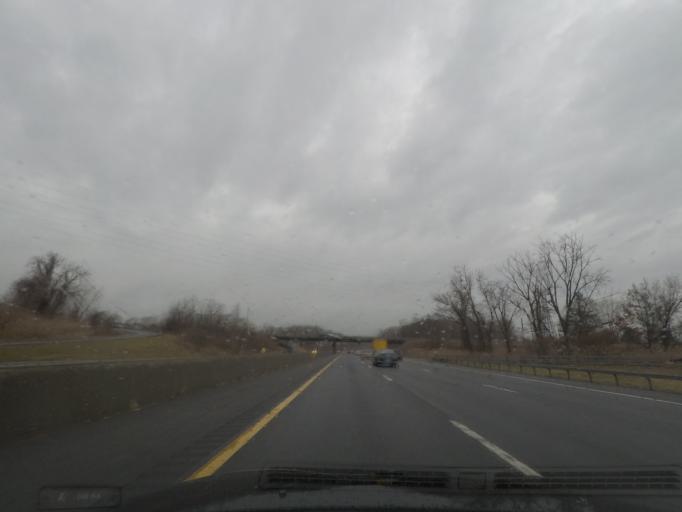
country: US
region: New York
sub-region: Albany County
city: Roessleville
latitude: 42.6872
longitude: -73.8074
